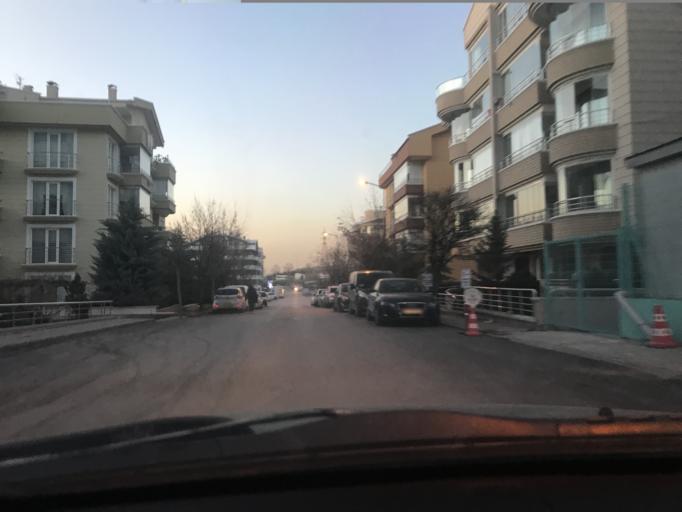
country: TR
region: Ankara
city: Batikent
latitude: 39.9141
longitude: 32.7730
